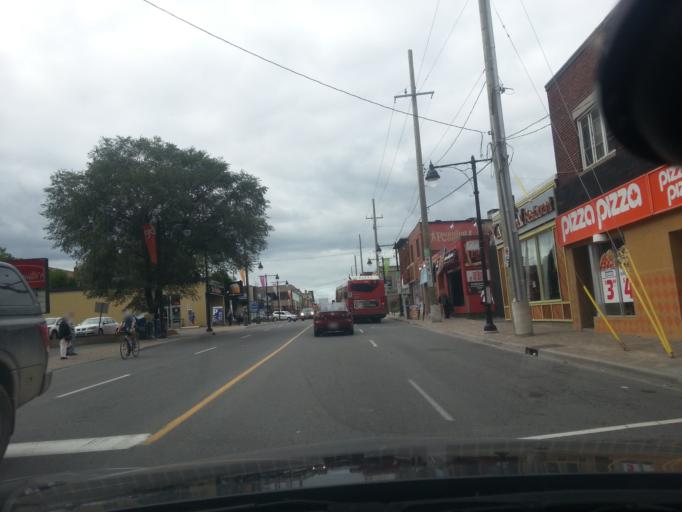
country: CA
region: Ontario
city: Ottawa
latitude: 45.3998
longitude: -75.6866
